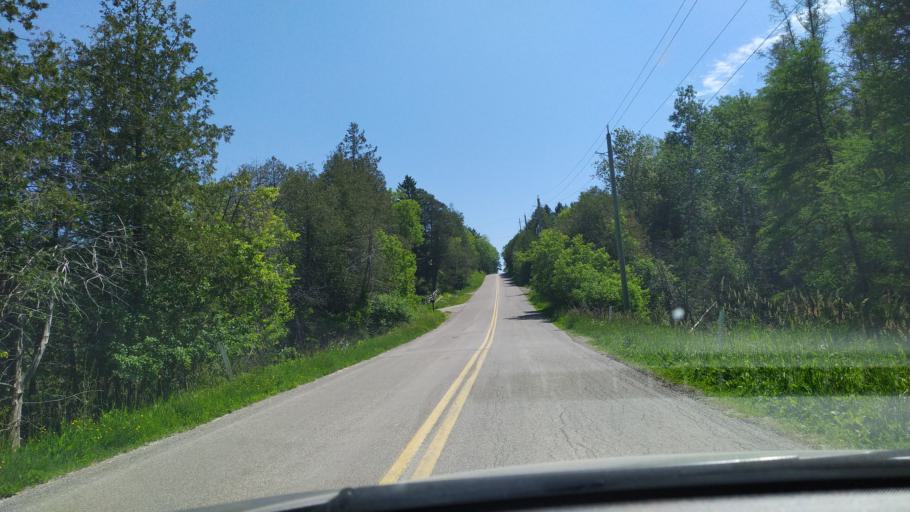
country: CA
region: Ontario
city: Waterloo
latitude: 43.4720
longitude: -80.6315
